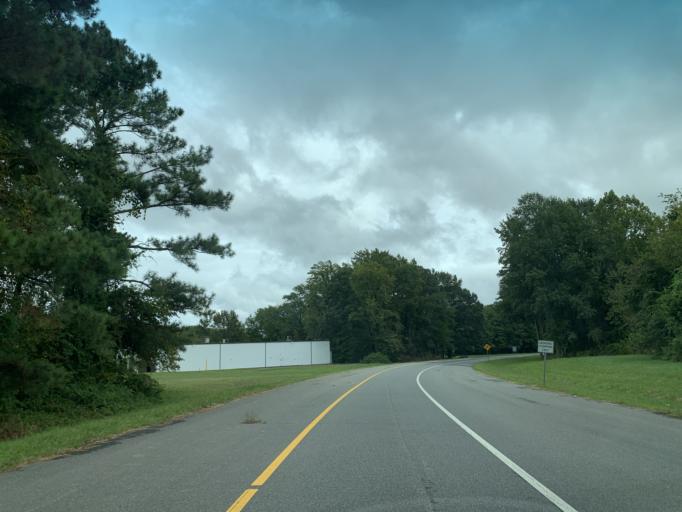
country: US
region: Maryland
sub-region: Caroline County
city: Denton
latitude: 38.8827
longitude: -75.8226
